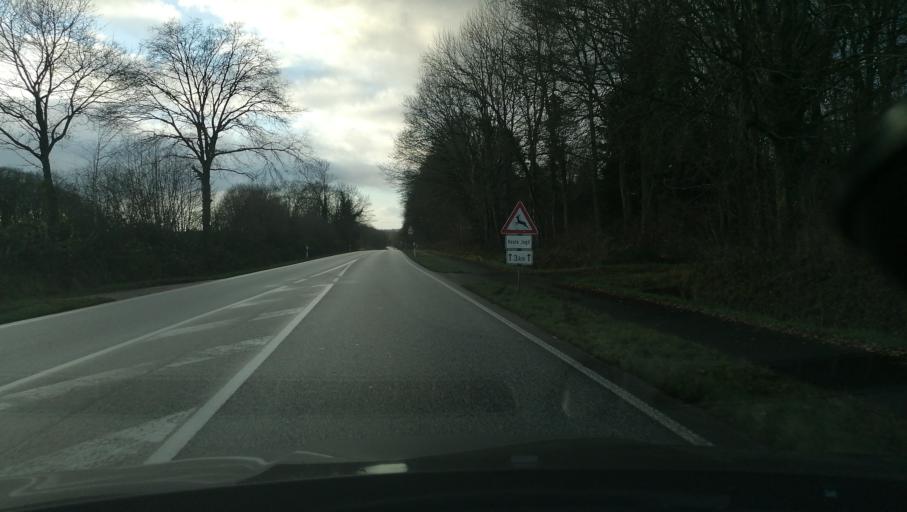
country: DE
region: Schleswig-Holstein
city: Tensbuttel-Rost
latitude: 54.1125
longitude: 9.2219
